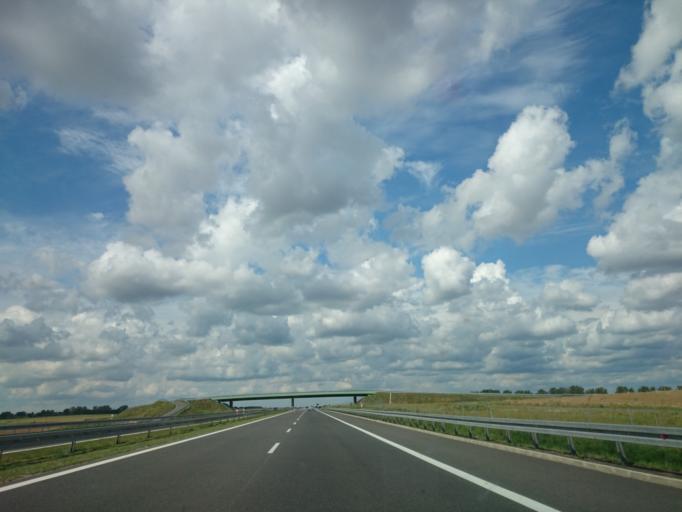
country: PL
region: Lubusz
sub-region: Powiat miedzyrzecki
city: Miedzyrzecz
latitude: 52.3570
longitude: 15.5533
